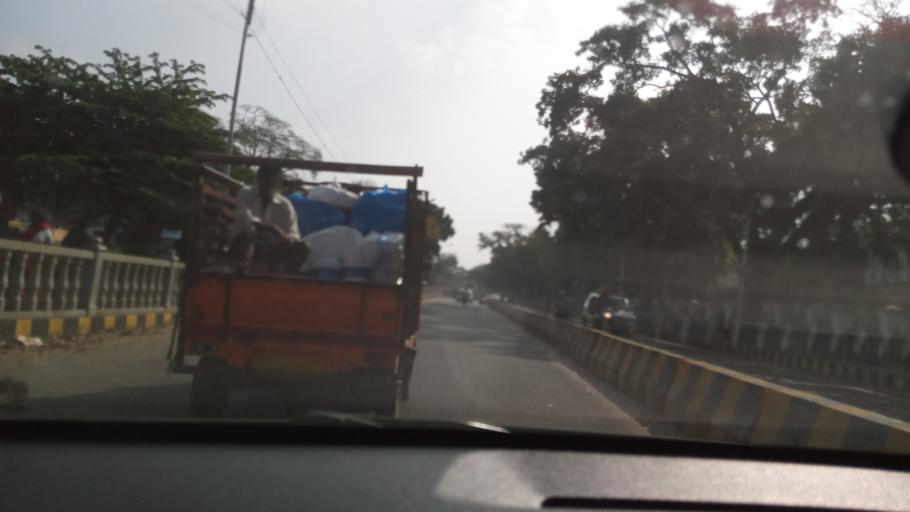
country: IN
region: Karnataka
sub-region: Mysore
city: Mysore
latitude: 12.3080
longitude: 76.6530
